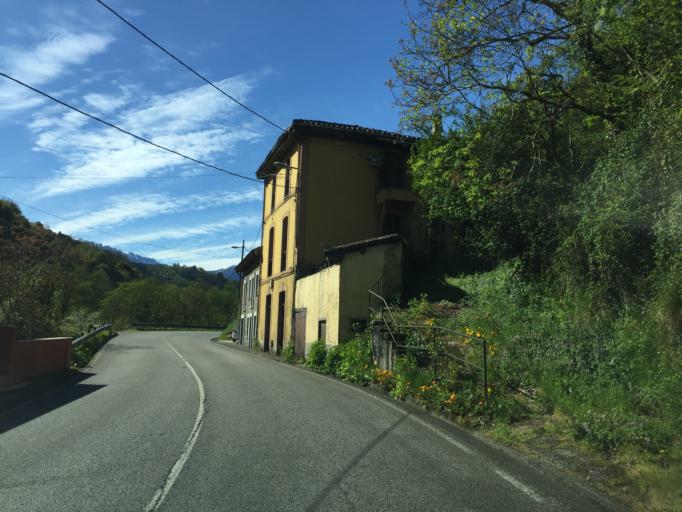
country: ES
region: Asturias
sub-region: Province of Asturias
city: Proaza
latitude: 43.3360
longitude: -5.9865
